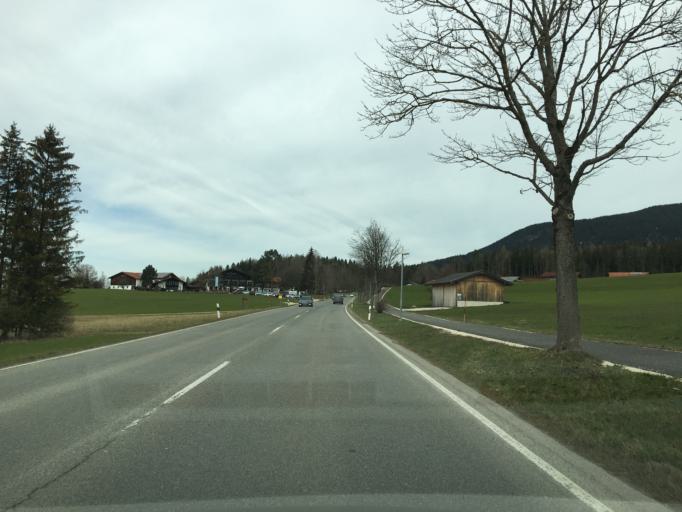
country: DE
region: Bavaria
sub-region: Upper Bavaria
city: Inzell
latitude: 47.7756
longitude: 12.7422
